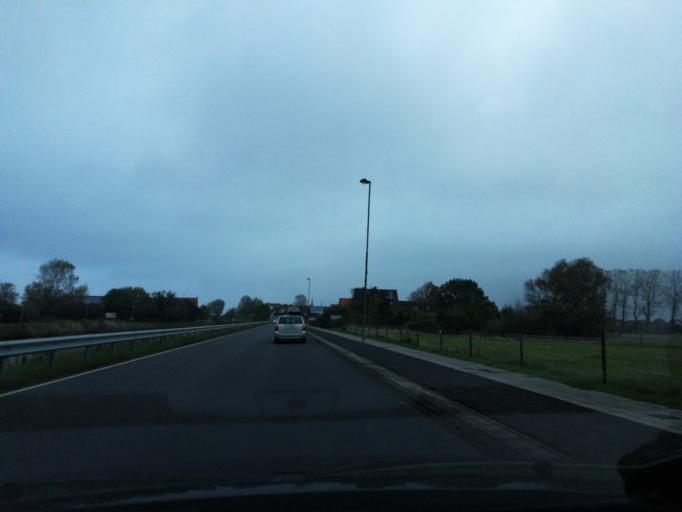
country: DE
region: Lower Saxony
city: Werdum
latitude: 53.6956
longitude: 7.8075
